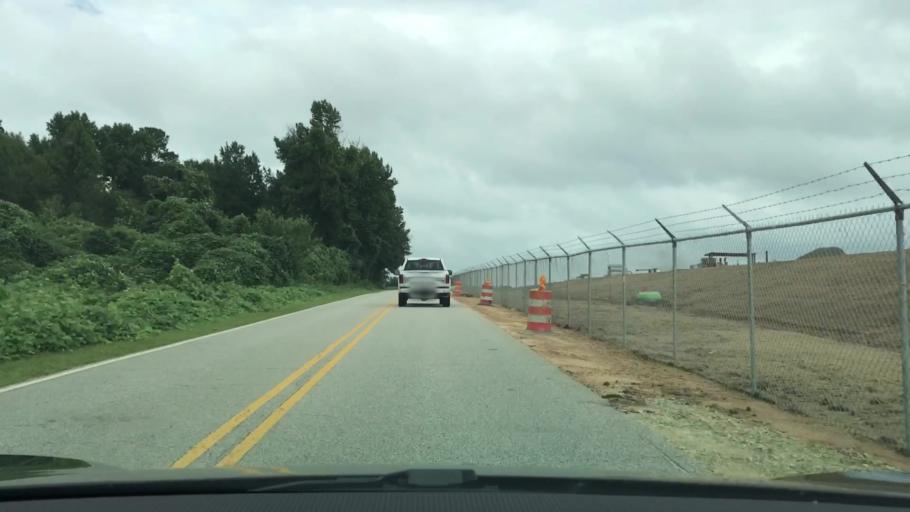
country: US
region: Alabama
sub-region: Lee County
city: Auburn
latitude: 32.6164
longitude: -85.4383
